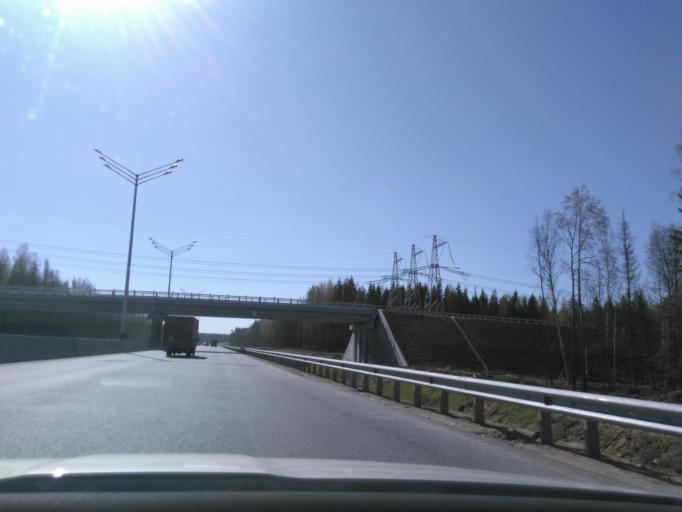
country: RU
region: Moskovskaya
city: Mendeleyevo
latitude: 56.0636
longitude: 37.2348
